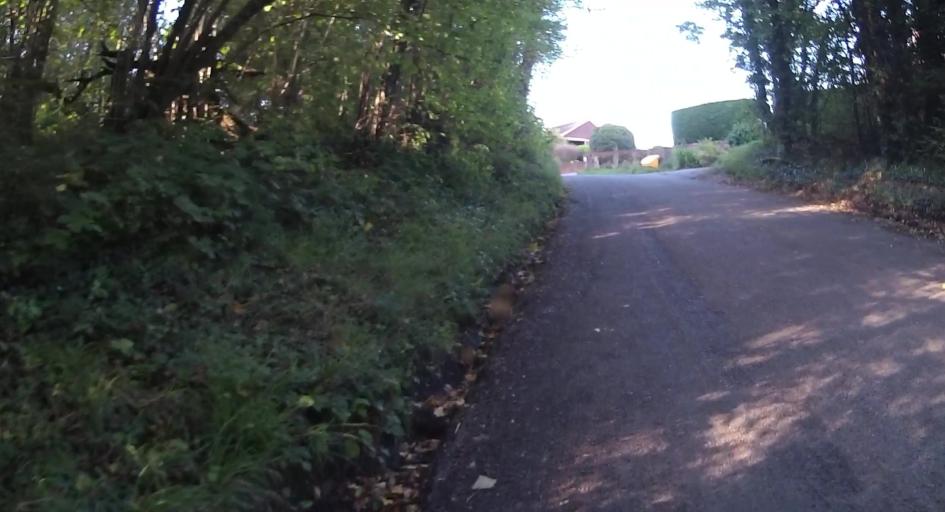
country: GB
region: England
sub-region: Surrey
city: Farnham
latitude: 51.2059
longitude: -0.8266
